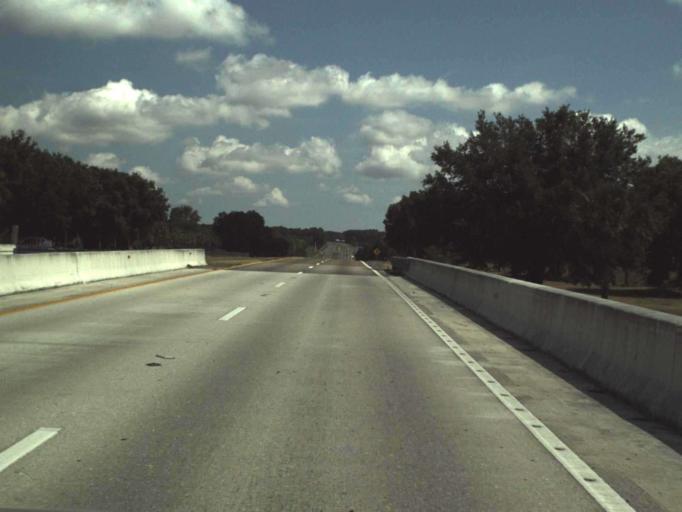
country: US
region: Florida
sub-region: Lake County
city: Mount Dora
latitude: 28.7968
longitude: -81.6250
